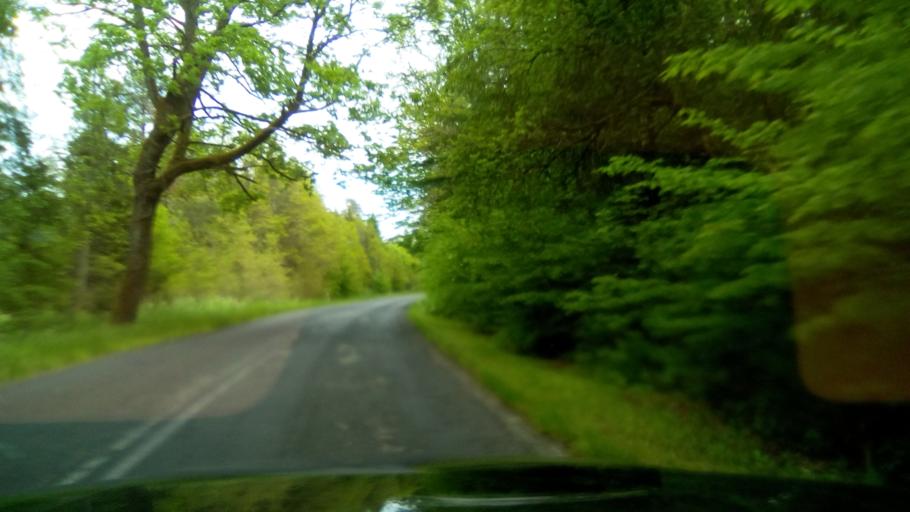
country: PL
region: Pomeranian Voivodeship
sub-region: Powiat bytowski
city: Czarna Dabrowka
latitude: 54.3783
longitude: 17.6356
